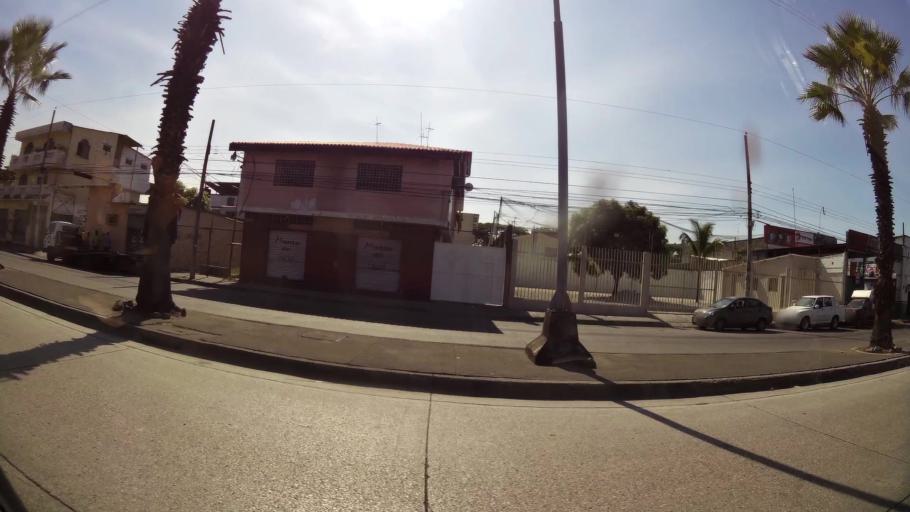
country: EC
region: Guayas
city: Eloy Alfaro
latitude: -2.1366
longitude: -79.9072
